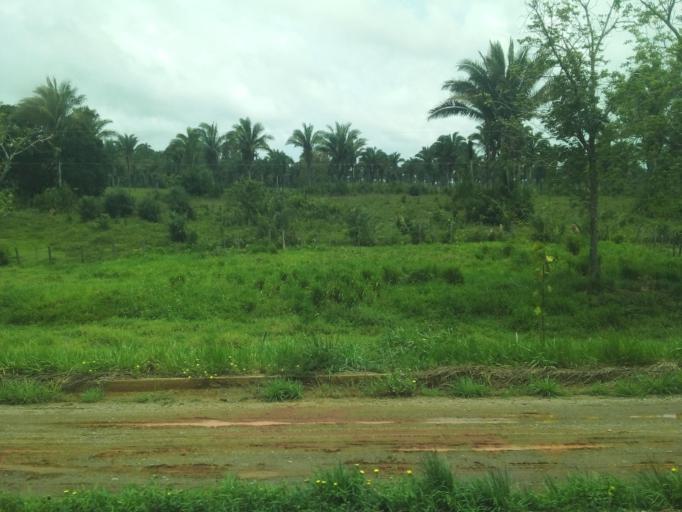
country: BR
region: Maranhao
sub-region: Vitoria Do Mearim
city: Vitoria do Mearim
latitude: -3.5324
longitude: -44.8644
